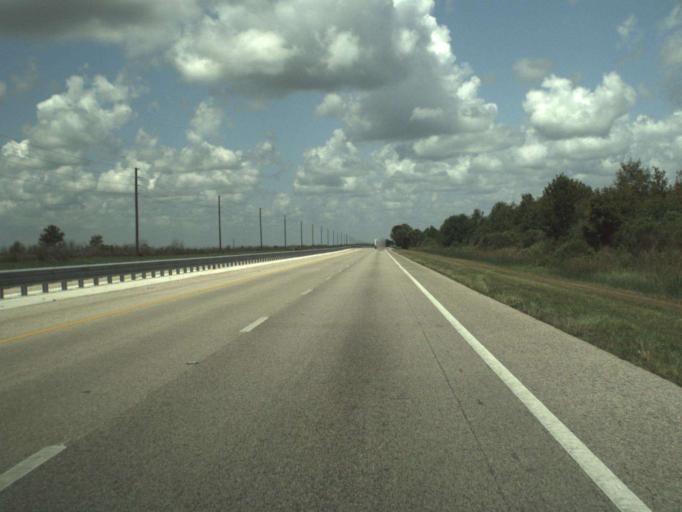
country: US
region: Florida
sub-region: Indian River County
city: Fellsmere
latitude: 27.6412
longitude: -80.7126
